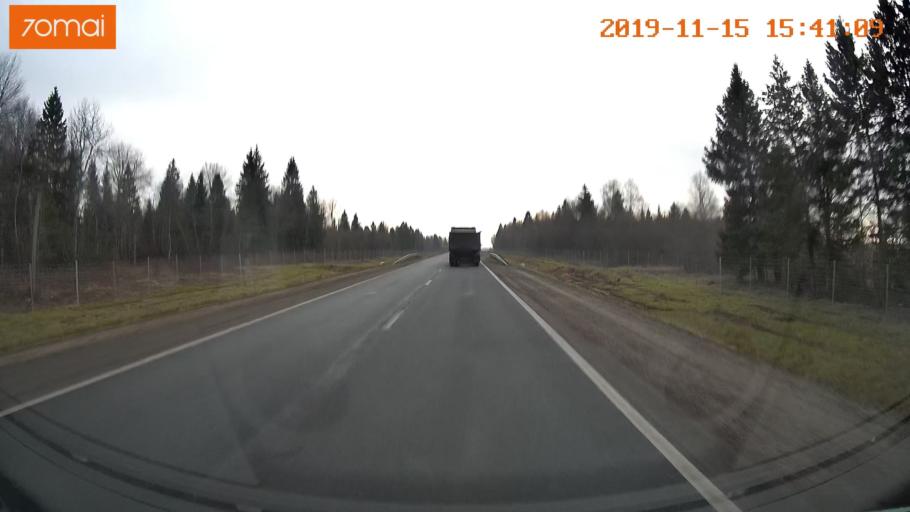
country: RU
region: Jaroslavl
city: Danilov
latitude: 58.0038
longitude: 40.0504
